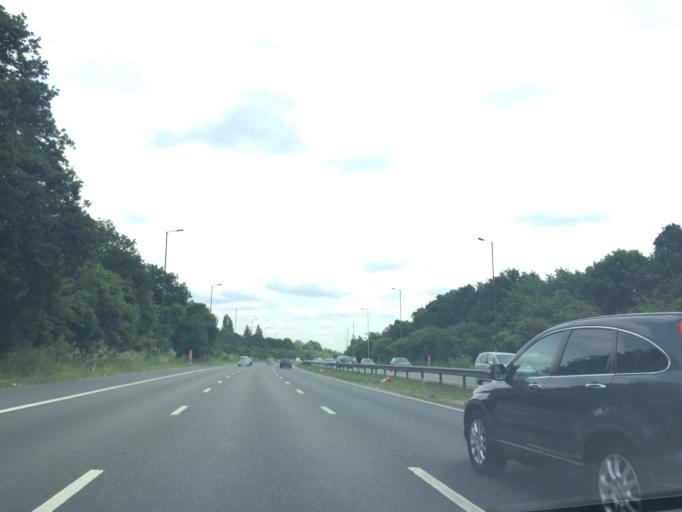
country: GB
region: England
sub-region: Kent
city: Dartford
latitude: 51.4331
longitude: 0.1910
